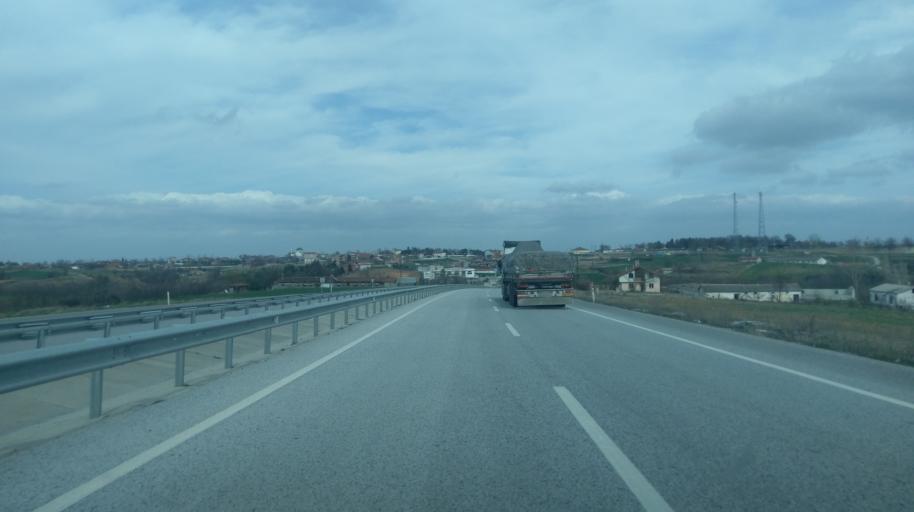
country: TR
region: Edirne
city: Kircasalih
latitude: 41.3843
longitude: 26.7927
